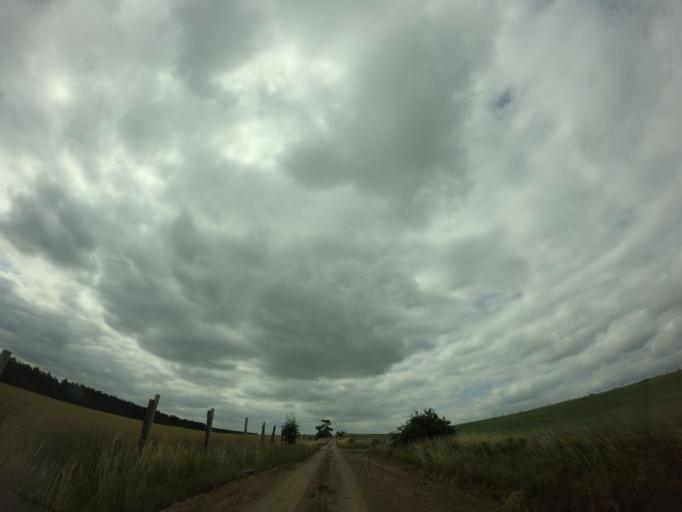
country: PL
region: Lubusz
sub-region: Powiat strzelecko-drezdenecki
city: Strzelce Krajenskie
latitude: 52.9179
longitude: 15.5987
